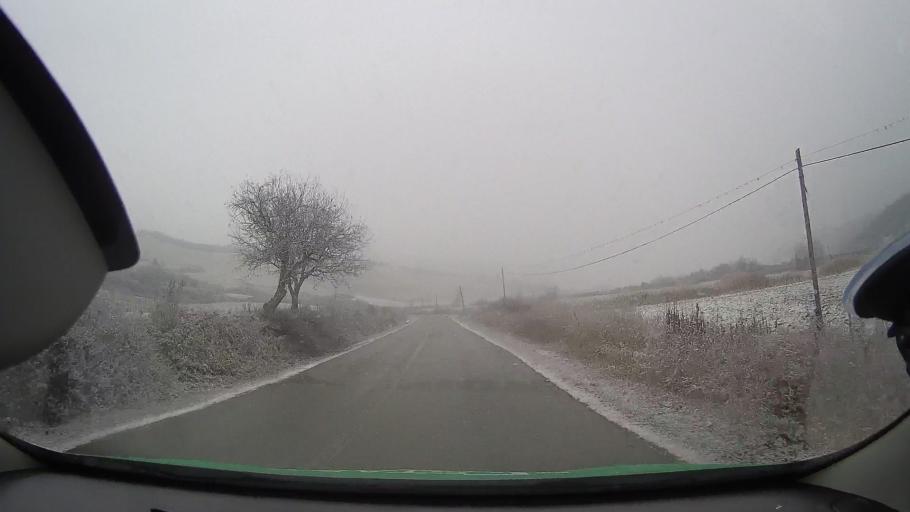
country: RO
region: Alba
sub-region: Comuna Lopadea Noua
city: Lopadea Noua
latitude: 46.2953
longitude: 23.8424
